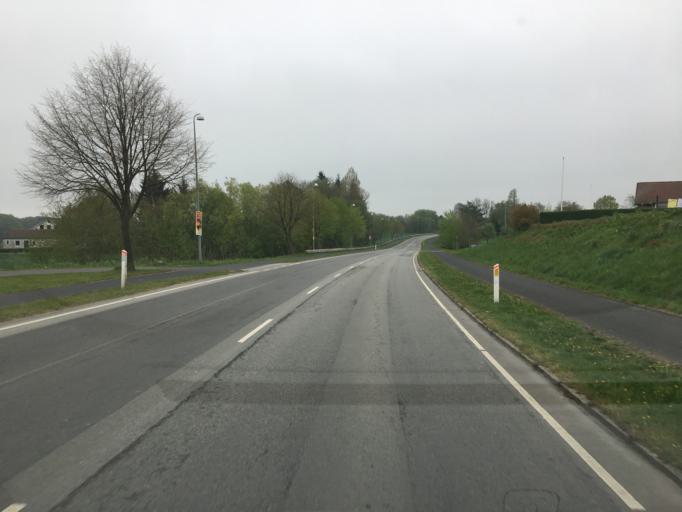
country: DK
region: South Denmark
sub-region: Aabenraa Kommune
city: Padborg
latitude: 54.8304
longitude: 9.3661
